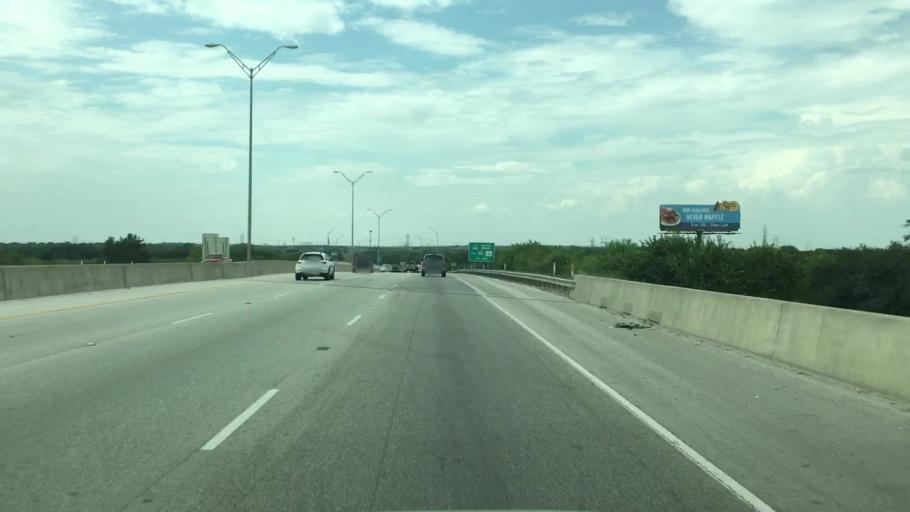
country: US
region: Texas
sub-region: Bexar County
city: China Grove
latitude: 29.3158
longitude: -98.4063
